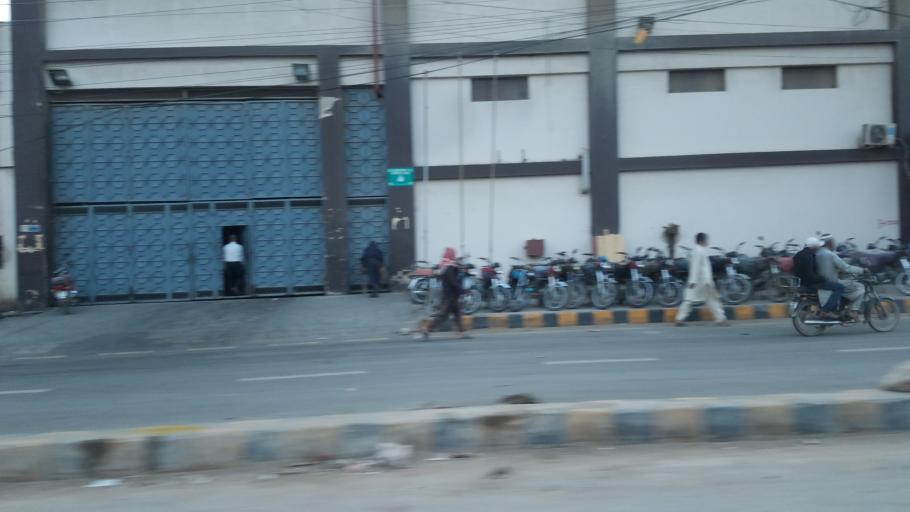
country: PK
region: Sindh
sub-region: Karachi District
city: Karachi
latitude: 24.9380
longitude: 67.0853
